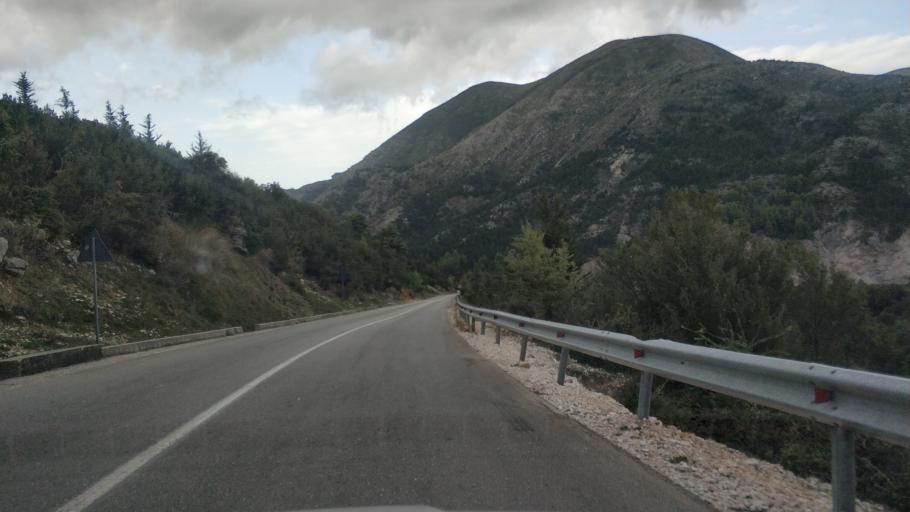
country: AL
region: Vlore
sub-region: Rrethi i Vlores
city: Orikum
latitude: 40.2419
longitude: 19.5514
